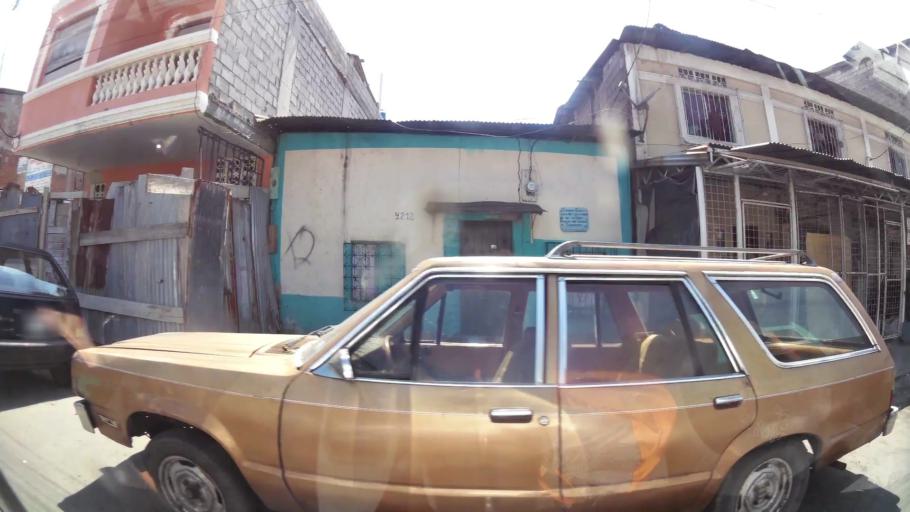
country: EC
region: Guayas
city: Guayaquil
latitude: -2.1960
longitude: -79.9129
